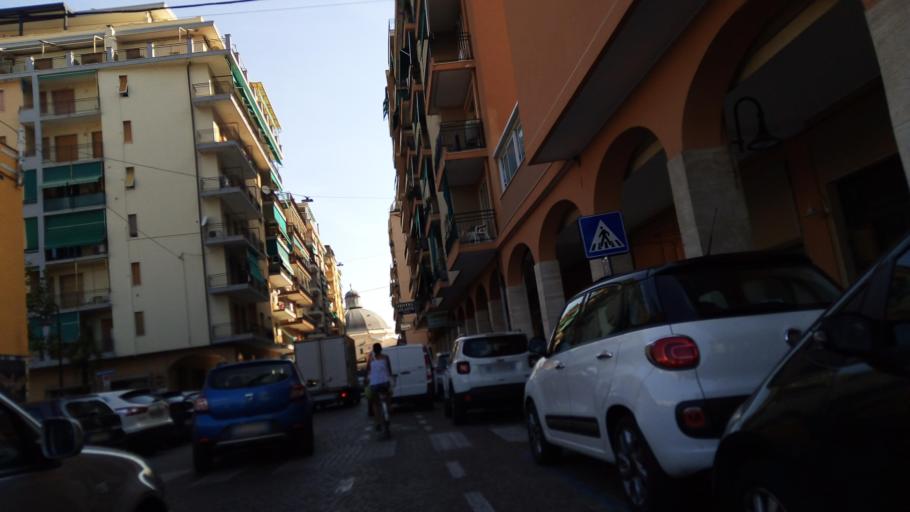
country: IT
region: Liguria
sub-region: Provincia di Savona
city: Loano
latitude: 44.1263
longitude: 8.2578
